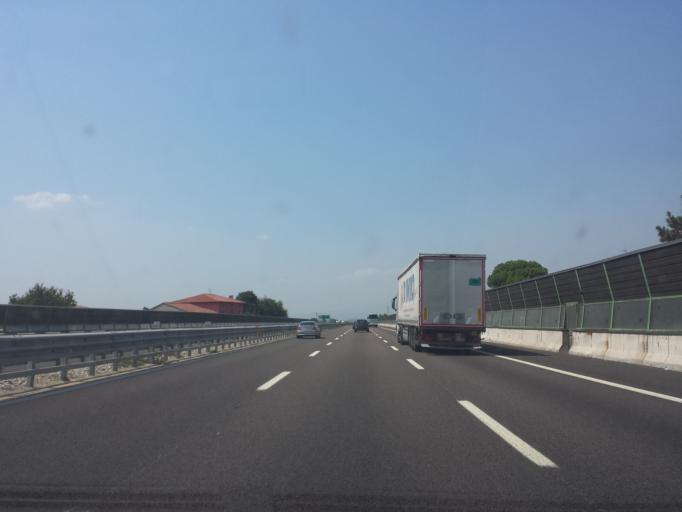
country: IT
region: Veneto
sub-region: Provincia di Vicenza
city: Grisignano di Zocco
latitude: 45.4805
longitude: 11.7003
